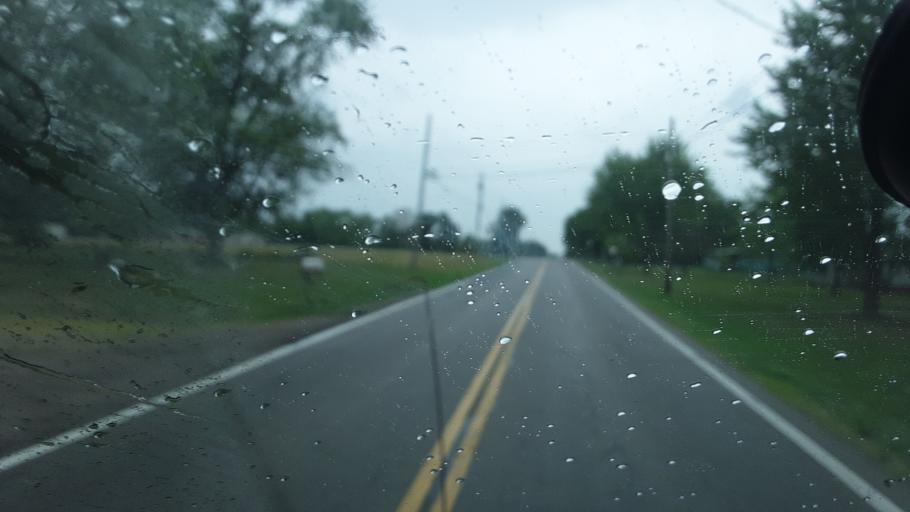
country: US
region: Ohio
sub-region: Williams County
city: Bryan
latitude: 41.5043
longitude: -84.6131
